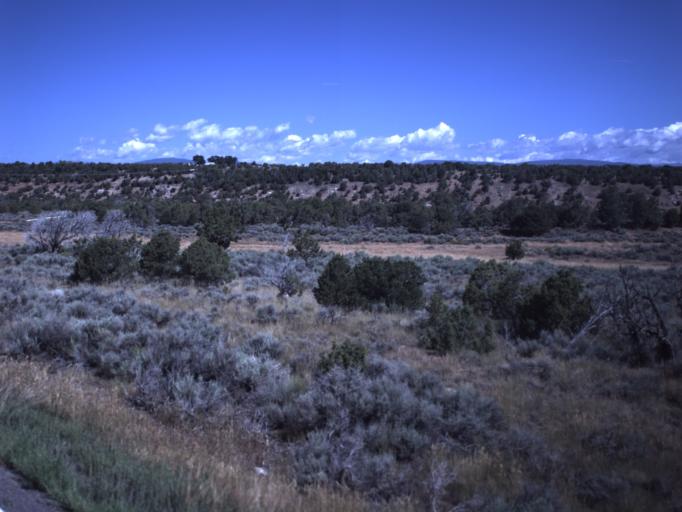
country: US
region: Utah
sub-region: Duchesne County
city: Duchesne
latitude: 40.3178
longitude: -110.3925
